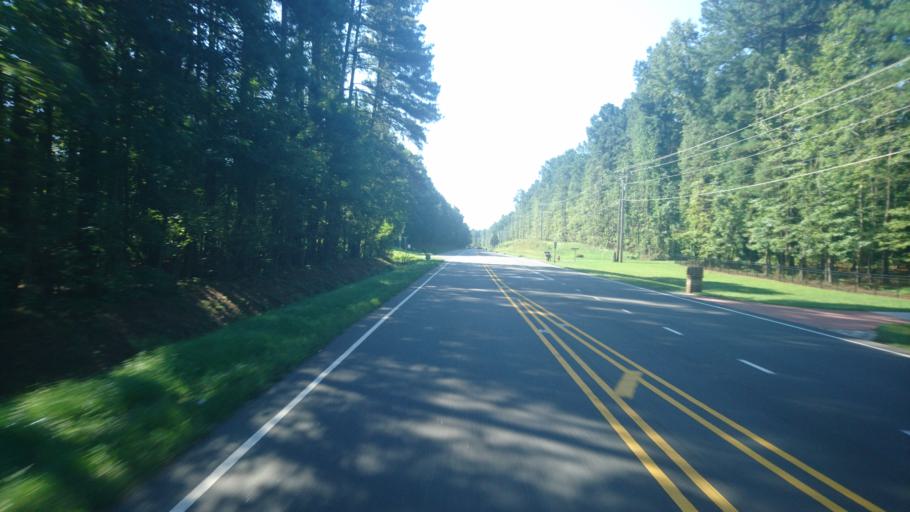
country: US
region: North Carolina
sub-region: Orange County
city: Hillsborough
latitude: 36.0283
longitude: -79.0803
